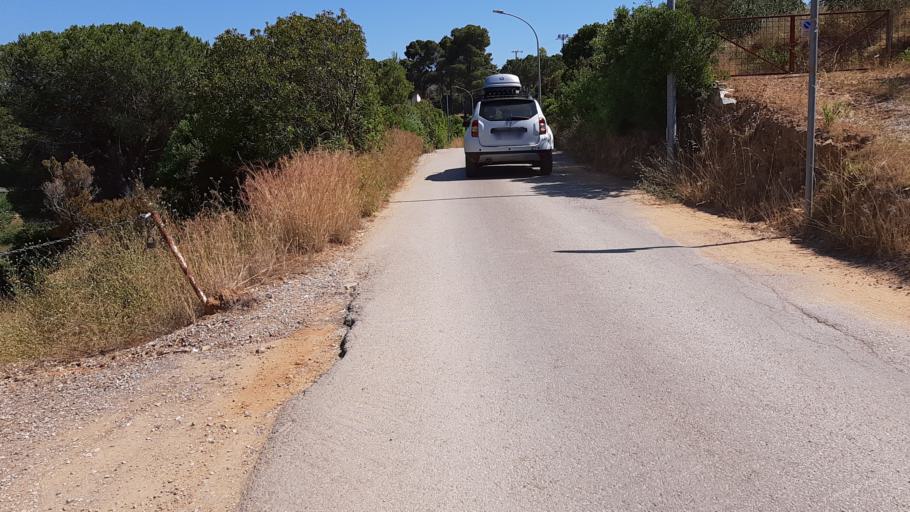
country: IT
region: Tuscany
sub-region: Provincia di Livorno
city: Portoferraio
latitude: 42.7605
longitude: 10.2977
